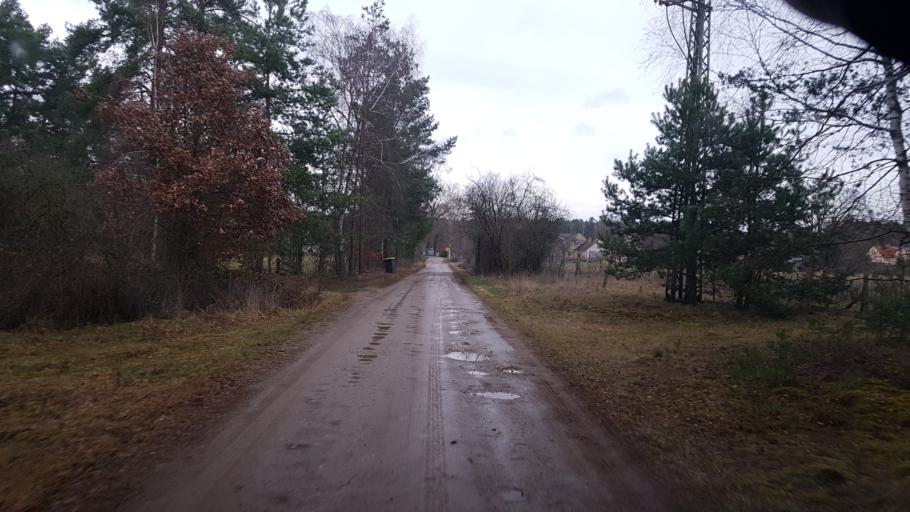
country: DE
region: Brandenburg
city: Sallgast
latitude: 51.6639
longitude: 13.8259
